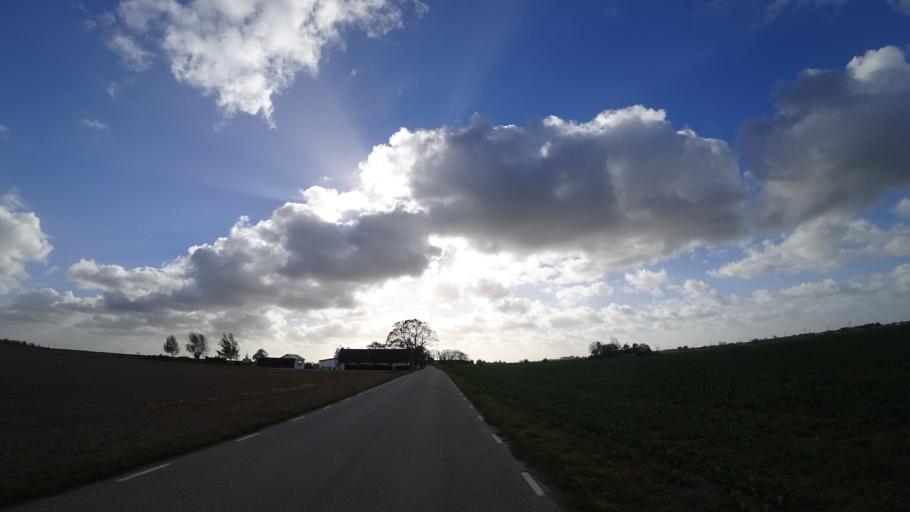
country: SE
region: Skane
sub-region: Staffanstorps Kommun
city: Hjaerup
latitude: 55.6558
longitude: 13.1594
